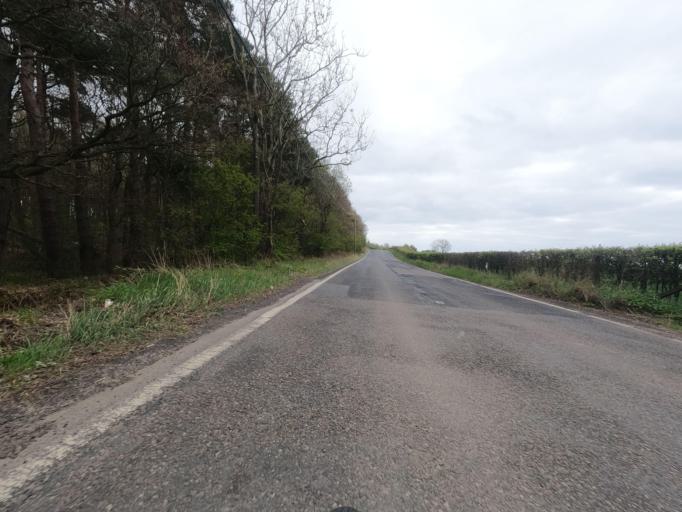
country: GB
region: England
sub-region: Newcastle upon Tyne
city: Dinnington
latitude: 55.0661
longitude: -1.6865
